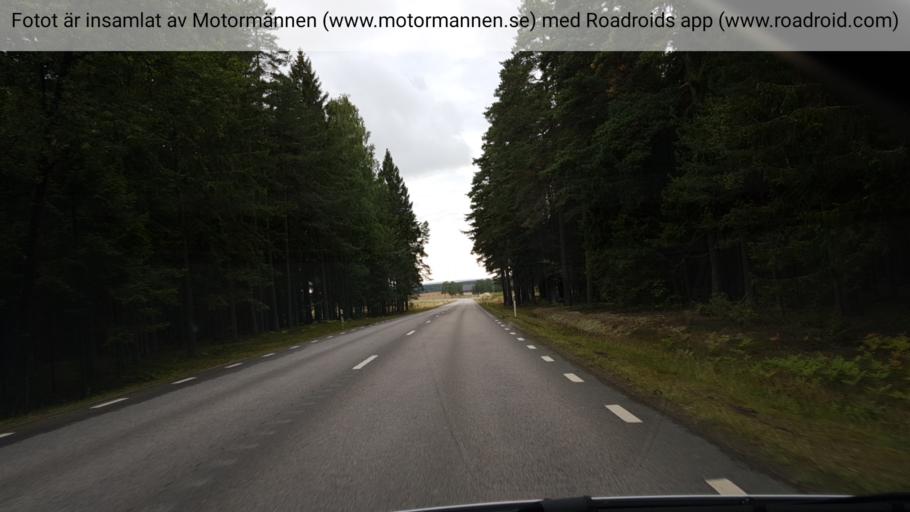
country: SE
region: Vaestra Goetaland
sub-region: Tibro Kommun
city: Tibro
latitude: 58.3441
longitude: 14.1539
